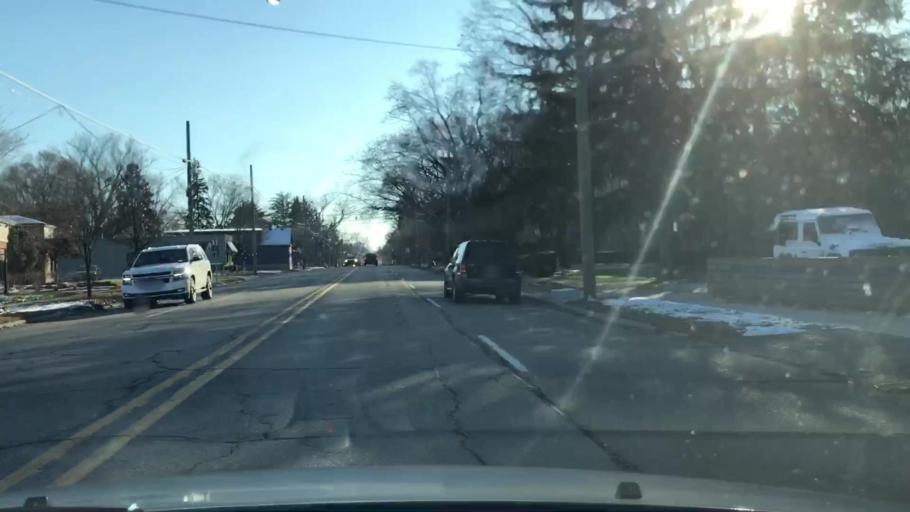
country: US
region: Michigan
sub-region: Oakland County
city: Clawson
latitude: 42.5124
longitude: -83.1411
